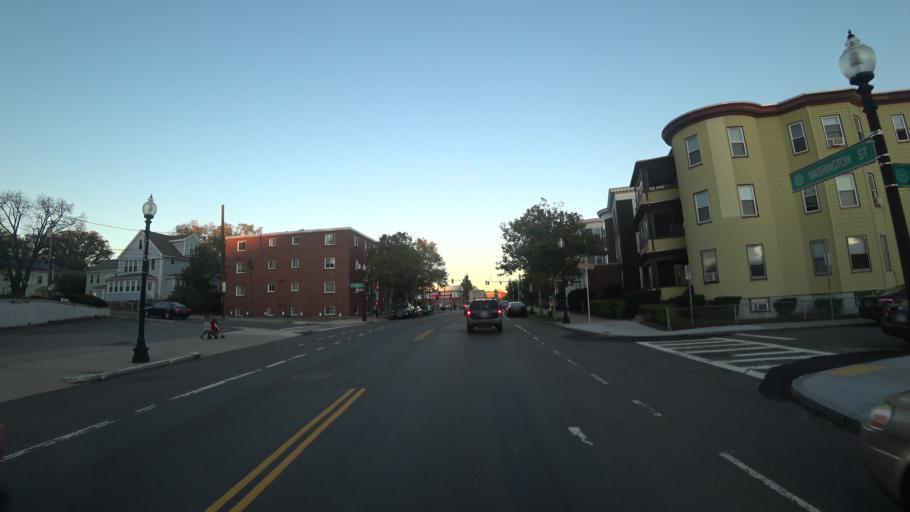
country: US
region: Massachusetts
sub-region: Middlesex County
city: Watertown
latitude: 42.3490
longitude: -71.1582
